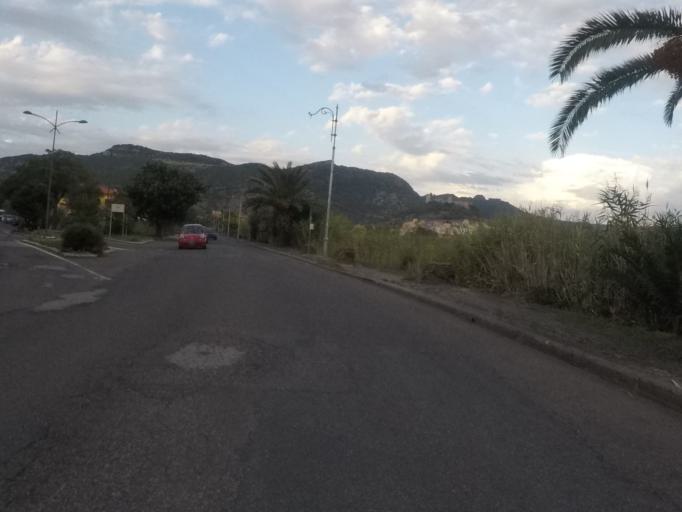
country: IT
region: Sardinia
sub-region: Provincia di Oristano
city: Bosa
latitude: 40.2929
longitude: 8.4931
